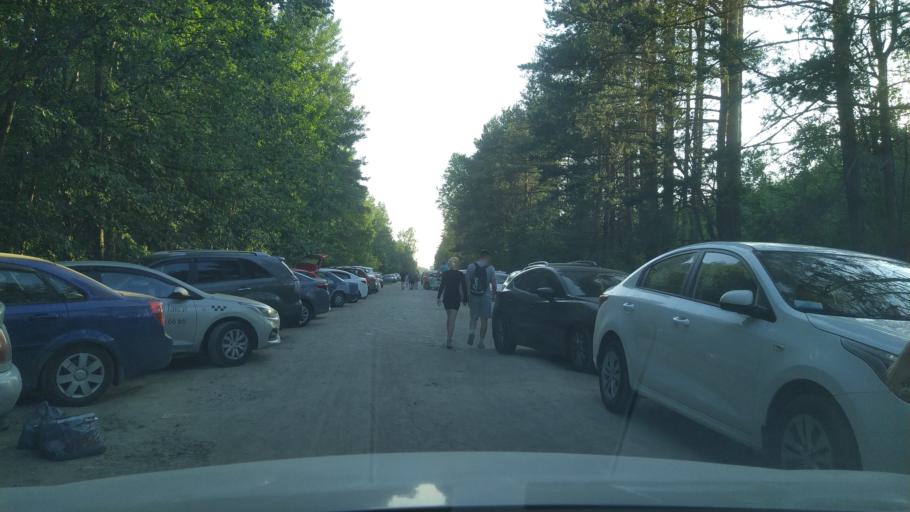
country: RU
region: Leningrad
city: Toksovo
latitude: 60.1136
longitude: 30.5179
